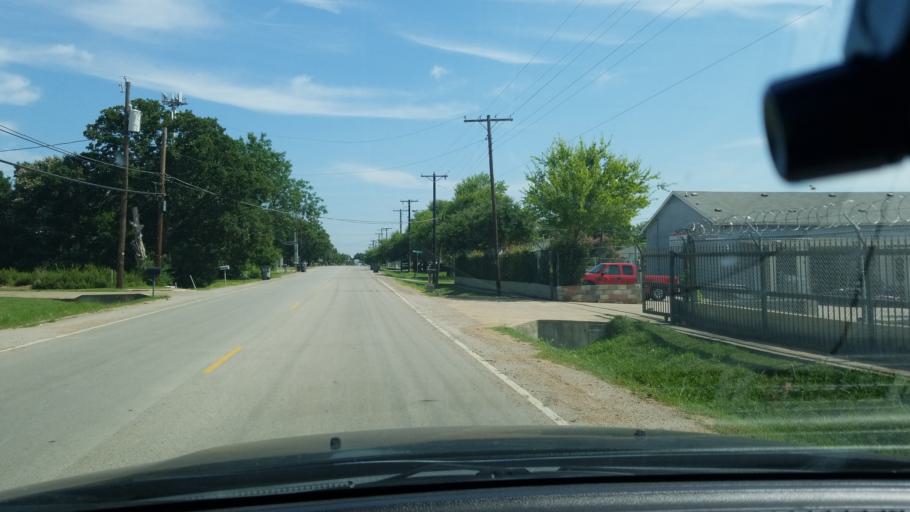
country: US
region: Texas
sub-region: Dallas County
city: Balch Springs
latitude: 32.7295
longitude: -96.6313
